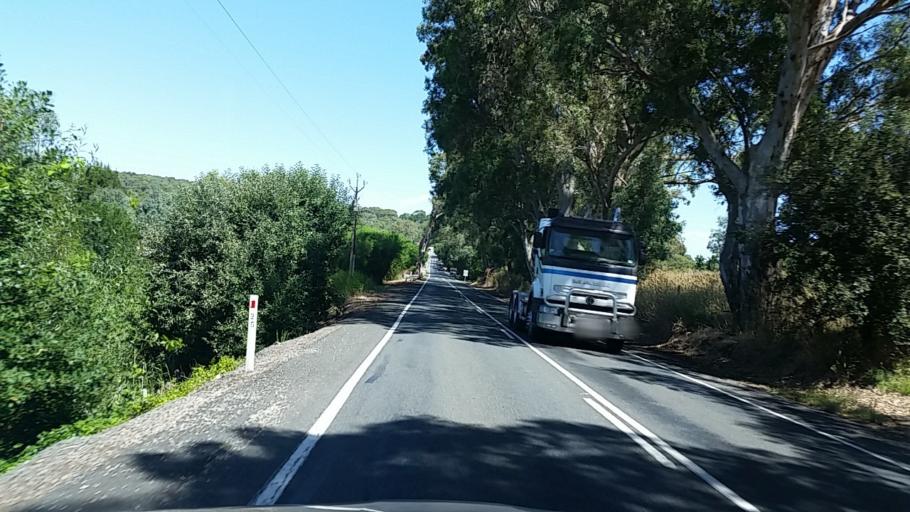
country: AU
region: South Australia
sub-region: Mount Barker
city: Little Hampton
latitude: -35.0436
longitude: 138.8642
